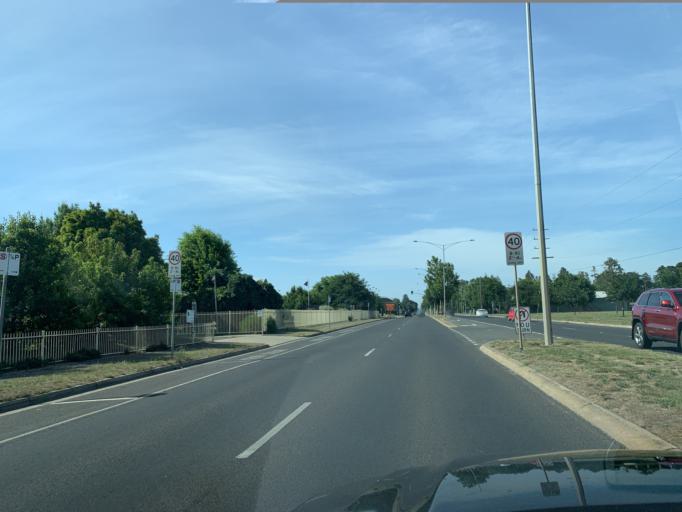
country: AU
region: Victoria
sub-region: Ballarat North
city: Newington
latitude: -37.5533
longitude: 143.8195
